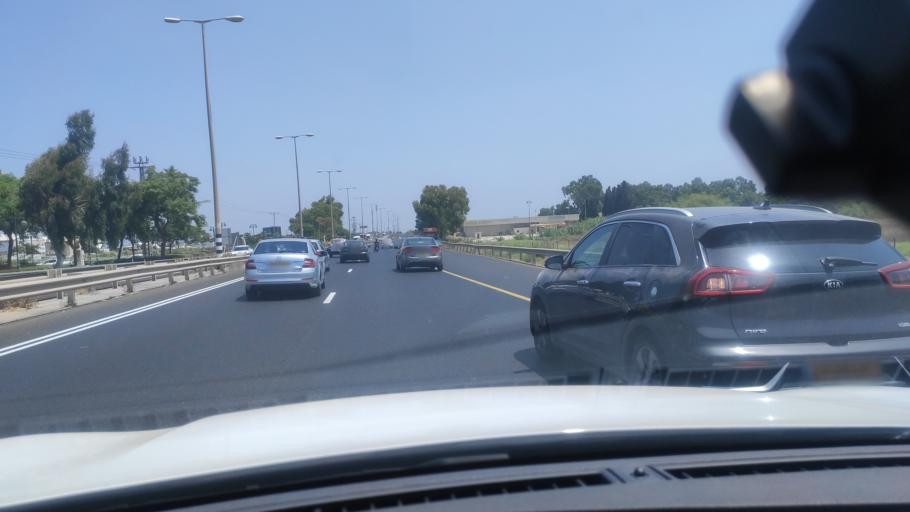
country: IL
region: Central District
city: Petah Tiqwa
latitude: 32.1049
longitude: 34.8994
